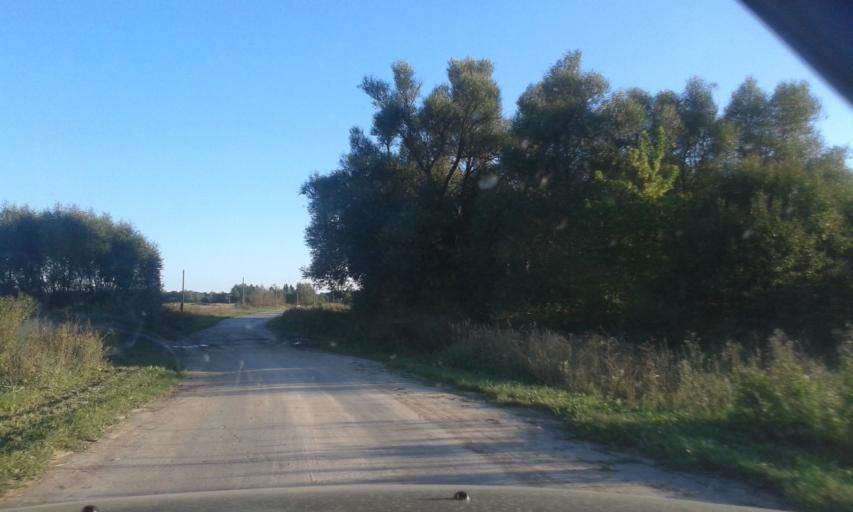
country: RU
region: Tula
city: Krapivna
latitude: 54.1213
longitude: 37.1530
